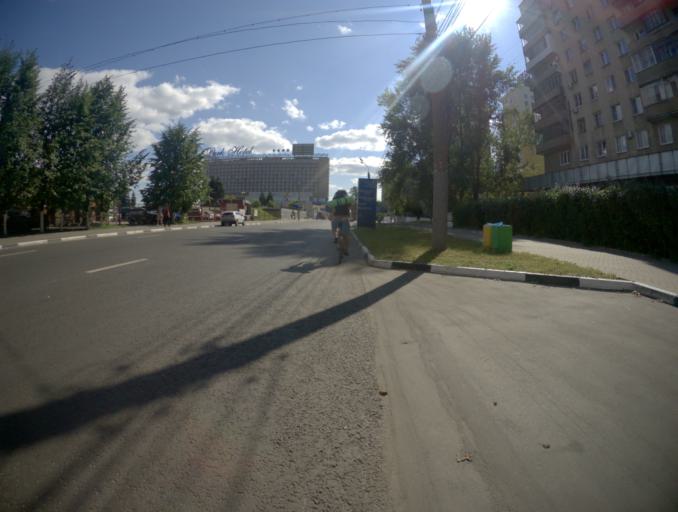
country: RU
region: Nizjnij Novgorod
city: Nizhniy Novgorod
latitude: 56.3277
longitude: 43.9594
